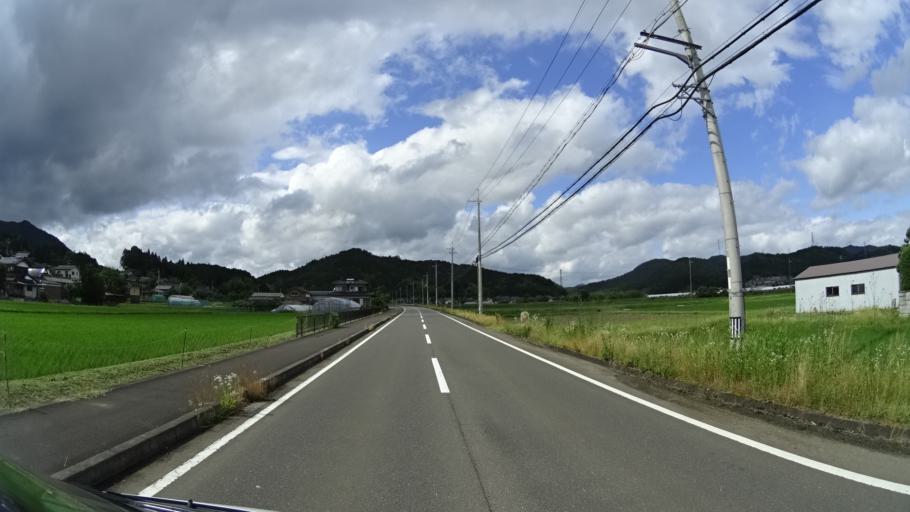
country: JP
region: Kyoto
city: Ayabe
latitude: 35.3262
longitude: 135.2078
